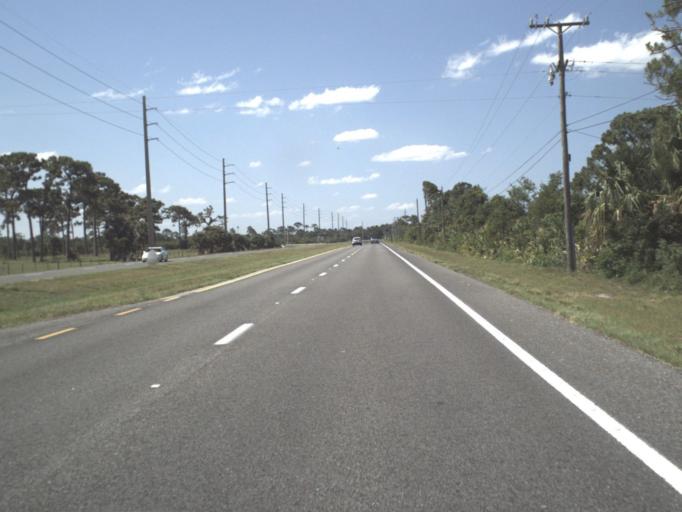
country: US
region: Florida
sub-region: Volusia County
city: Oak Hill
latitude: 28.7766
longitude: -80.8806
